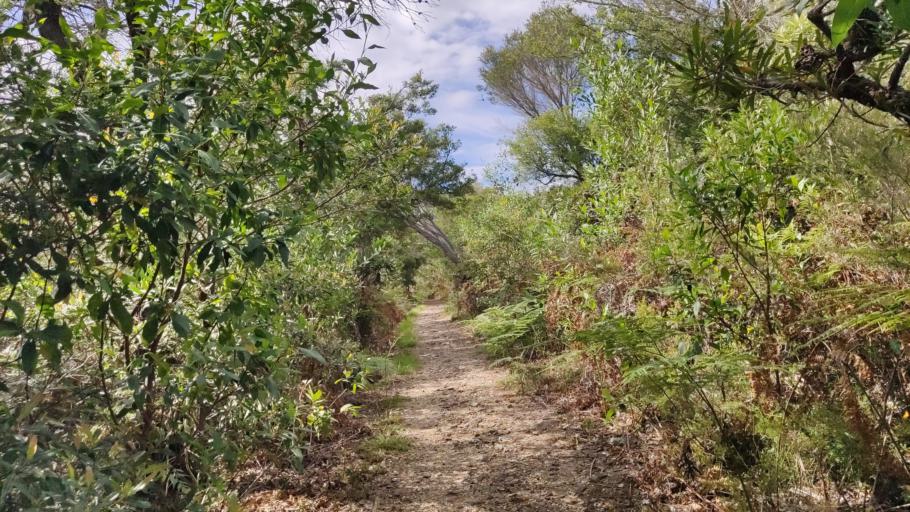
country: AU
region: New South Wales
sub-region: Port Macquarie-Hastings
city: North Haven
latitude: -31.6439
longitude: 152.8365
